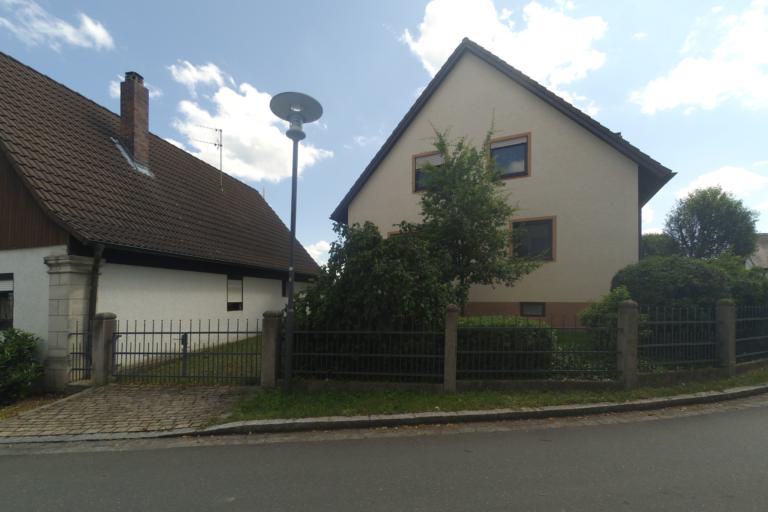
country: DE
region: Bavaria
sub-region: Upper Franconia
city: Hallerndorf
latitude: 49.7795
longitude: 10.9546
